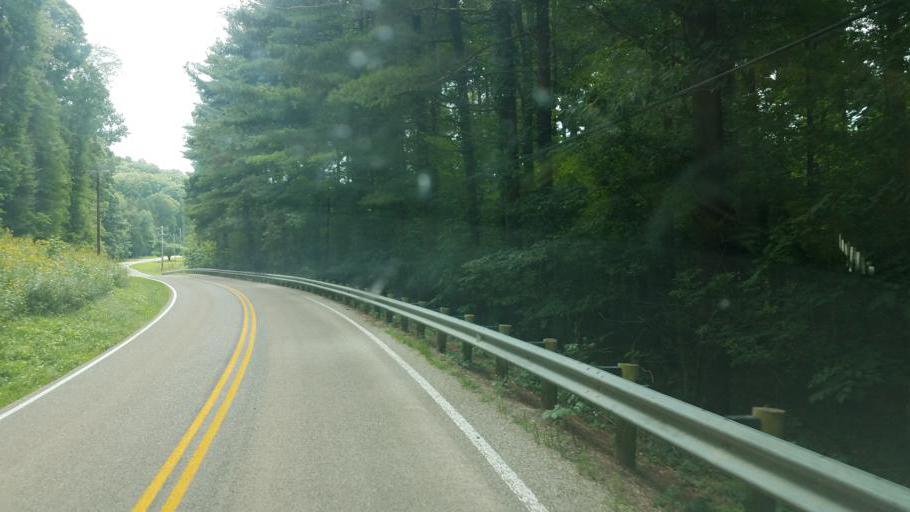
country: US
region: Ohio
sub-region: Ashland County
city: Loudonville
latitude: 40.6345
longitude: -82.3407
